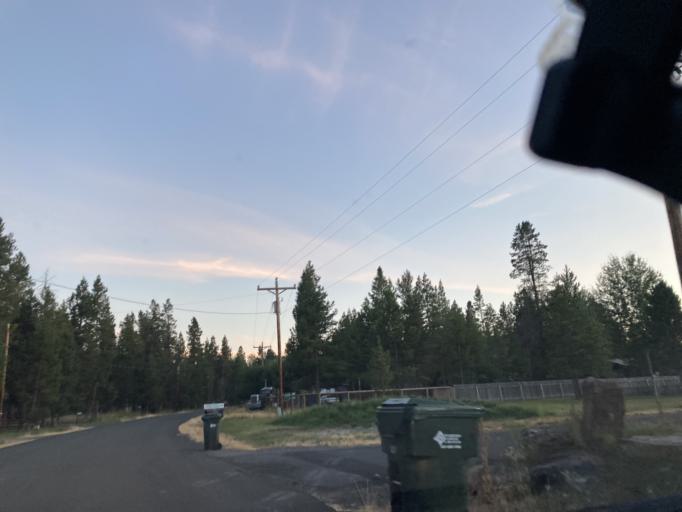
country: US
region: Oregon
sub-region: Deschutes County
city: Three Rivers
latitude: 43.8283
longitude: -121.4644
